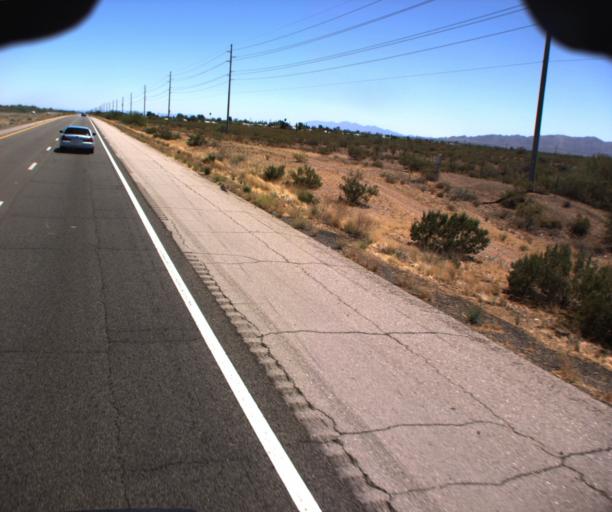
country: US
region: Arizona
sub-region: Maricopa County
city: Sun City West
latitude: 33.7941
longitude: -112.5497
